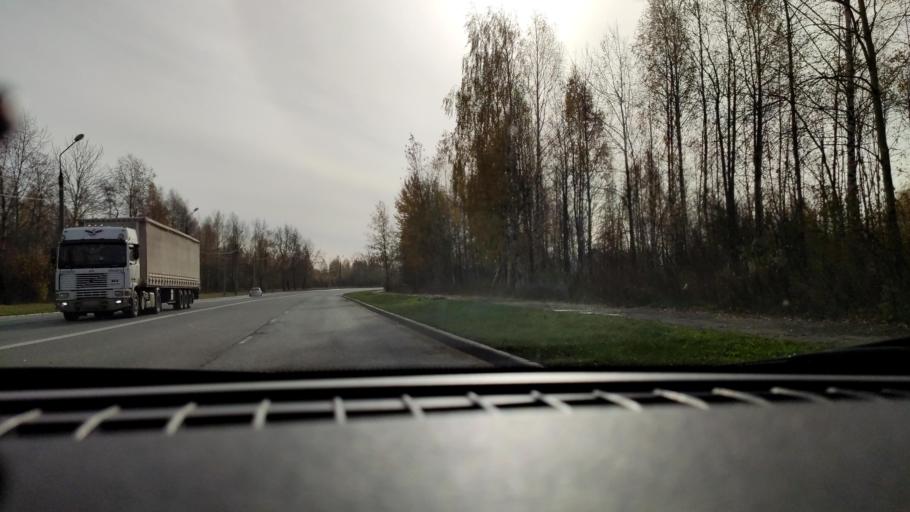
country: RU
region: Perm
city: Polazna
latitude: 58.1311
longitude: 56.4050
